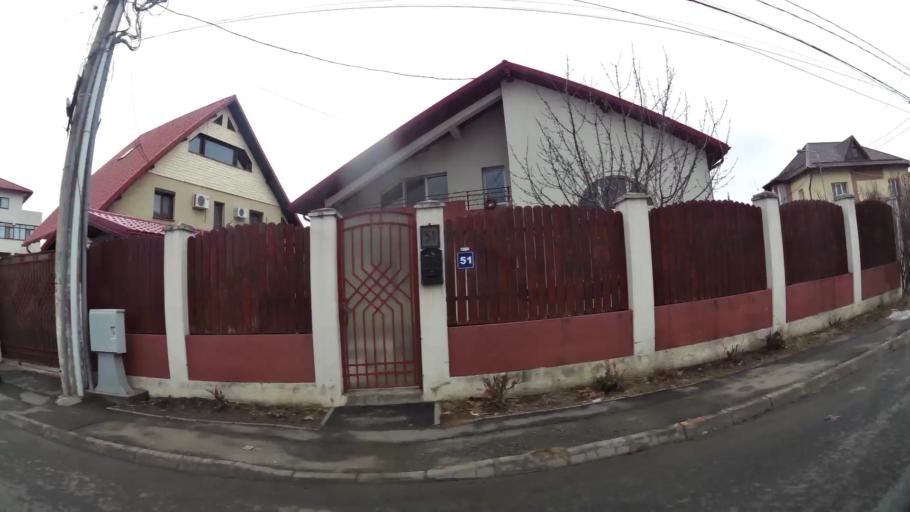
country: RO
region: Ilfov
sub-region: Comuna Otopeni
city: Otopeni
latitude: 44.5543
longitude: 26.0774
